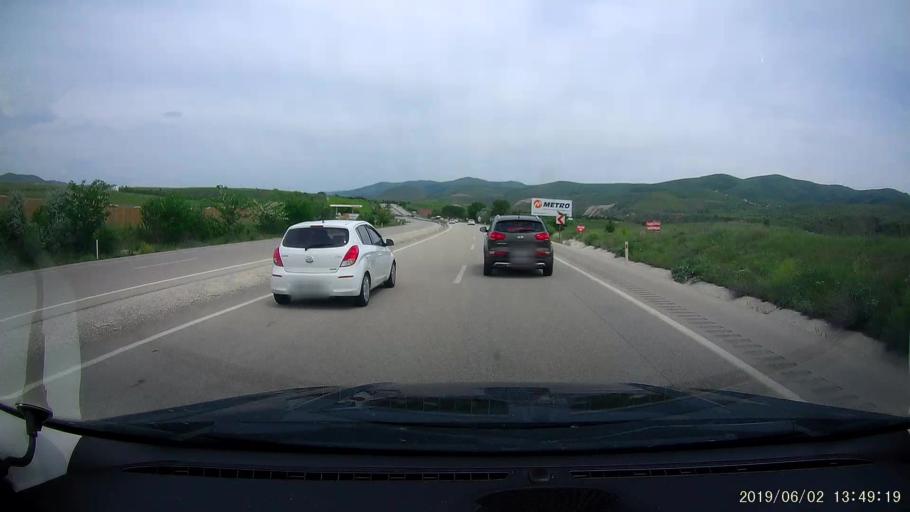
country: TR
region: Cankiri
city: Kursunlu
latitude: 40.8302
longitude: 33.3258
